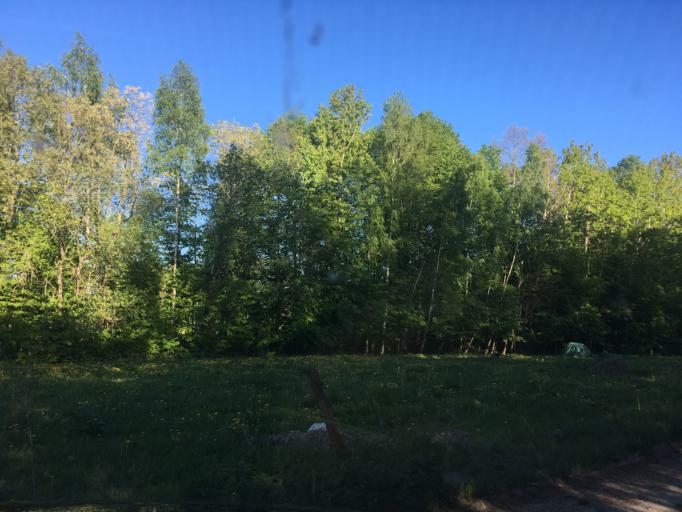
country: PL
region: Warmian-Masurian Voivodeship
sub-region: Powiat piski
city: Ruciane-Nida
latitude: 53.6555
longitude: 21.4833
